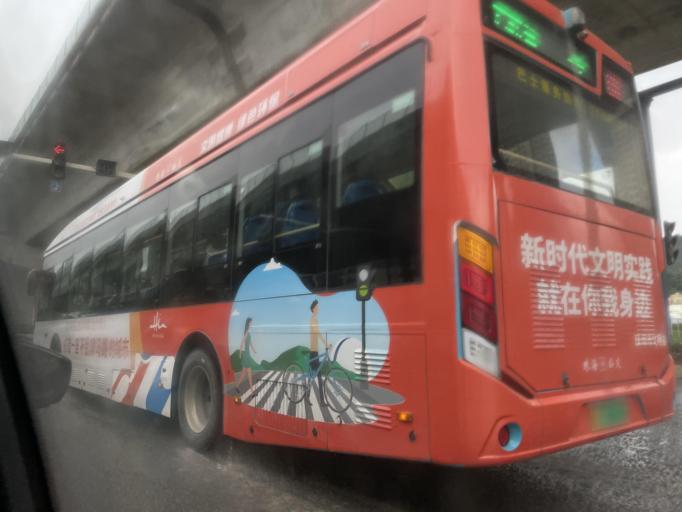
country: CN
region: Guangdong
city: Nanping
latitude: 22.1765
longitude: 113.4738
